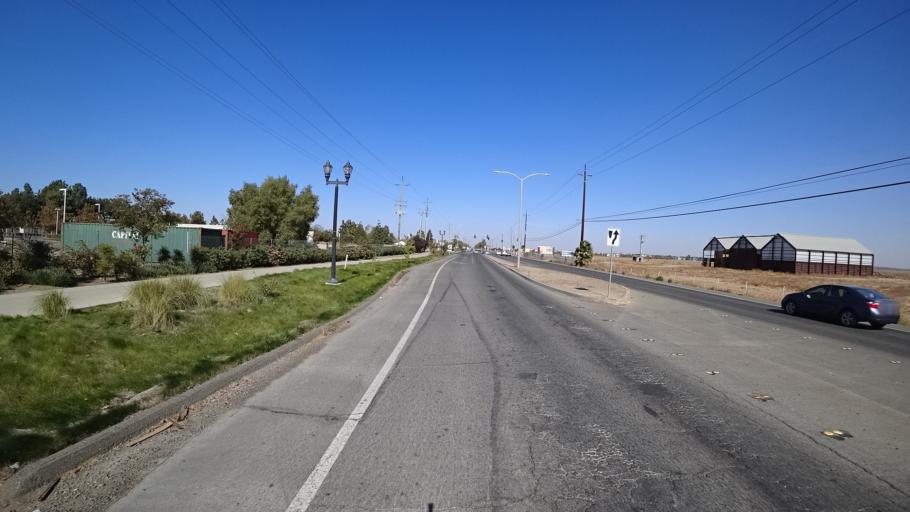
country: US
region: California
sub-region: Yolo County
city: Woodland
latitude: 38.6614
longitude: -121.7288
